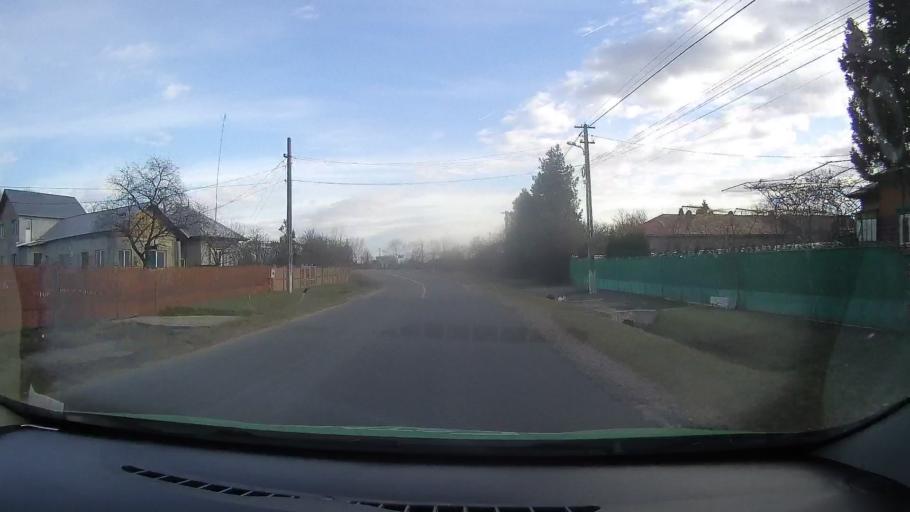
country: RO
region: Dambovita
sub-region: Municipiul Targoviste
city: Targoviste
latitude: 44.8906
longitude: 25.4617
